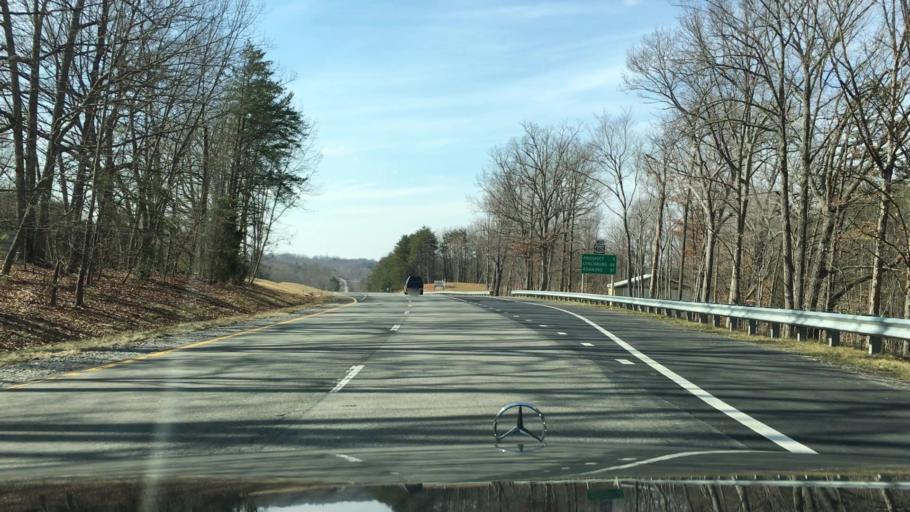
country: US
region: Virginia
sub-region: Prince Edward County
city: Hampden Sydney
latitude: 37.3162
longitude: -78.4726
